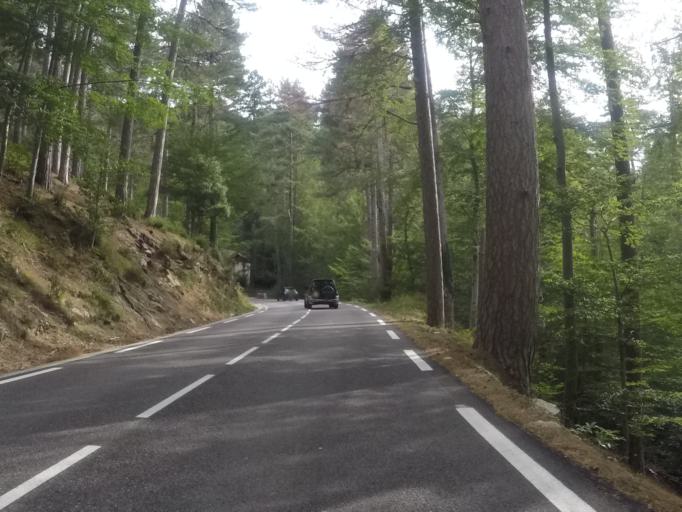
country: FR
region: Corsica
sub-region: Departement de la Haute-Corse
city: Corte
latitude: 42.1254
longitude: 9.1354
